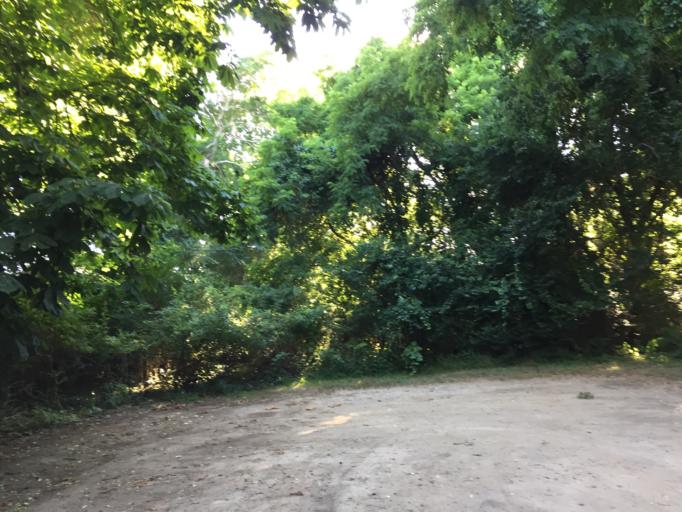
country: US
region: New York
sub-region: Suffolk County
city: Greenport
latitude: 41.1559
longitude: -72.2423
